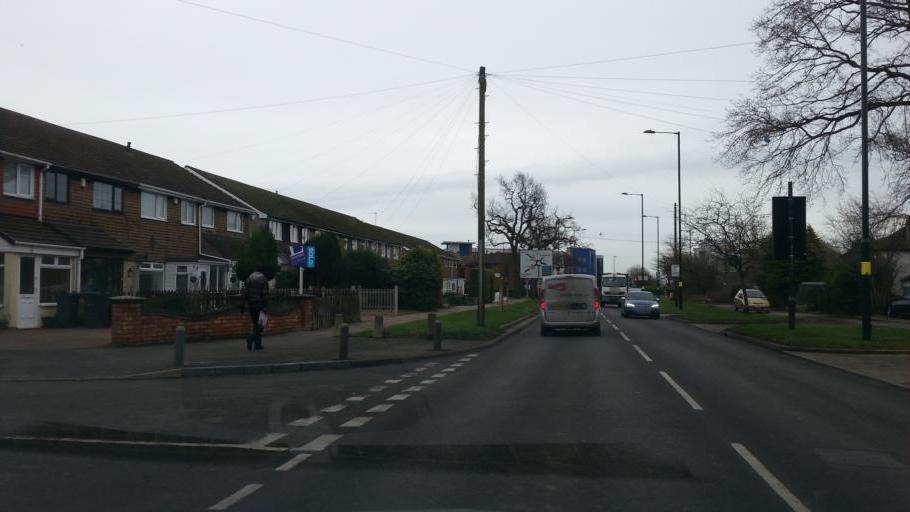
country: GB
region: England
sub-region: Solihull
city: Tidbury Green
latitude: 52.4045
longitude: -1.8894
